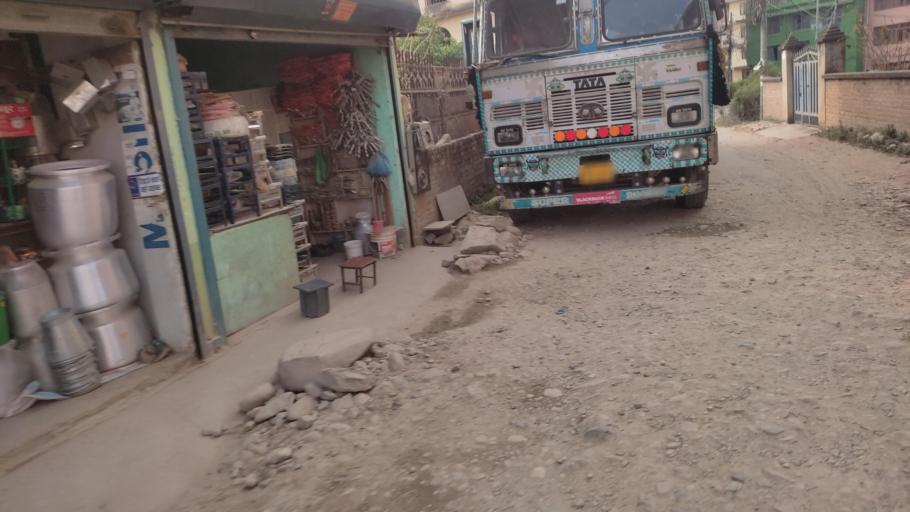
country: NP
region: Central Region
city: Kirtipur
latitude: 27.6708
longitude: 85.2803
